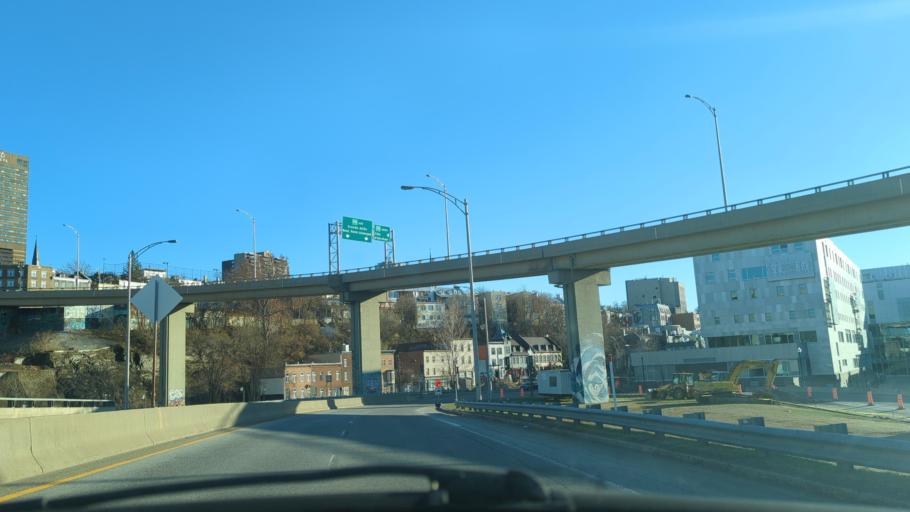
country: CA
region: Quebec
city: Quebec
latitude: 46.8150
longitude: -71.2176
